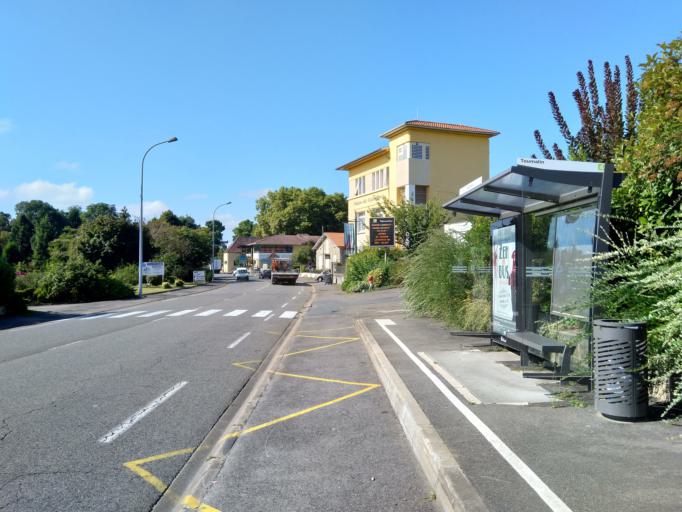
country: FR
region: Aquitaine
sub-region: Departement des Landes
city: Saint-Paul-les-Dax
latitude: 43.7265
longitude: -1.0503
